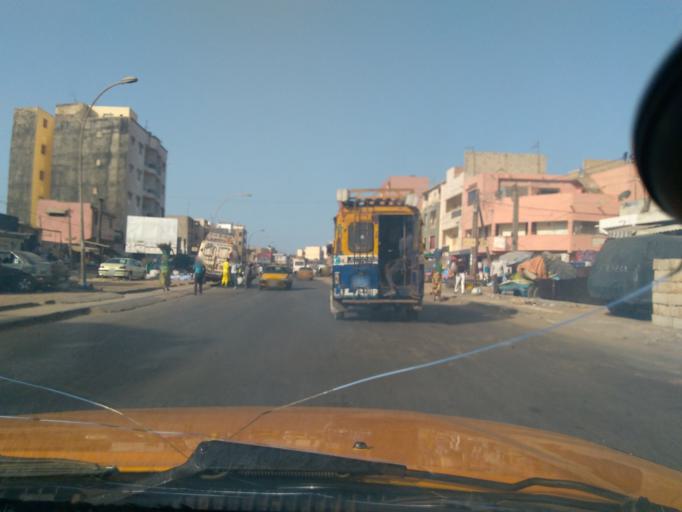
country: SN
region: Dakar
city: Grand Dakar
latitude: 14.7416
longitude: -17.4458
